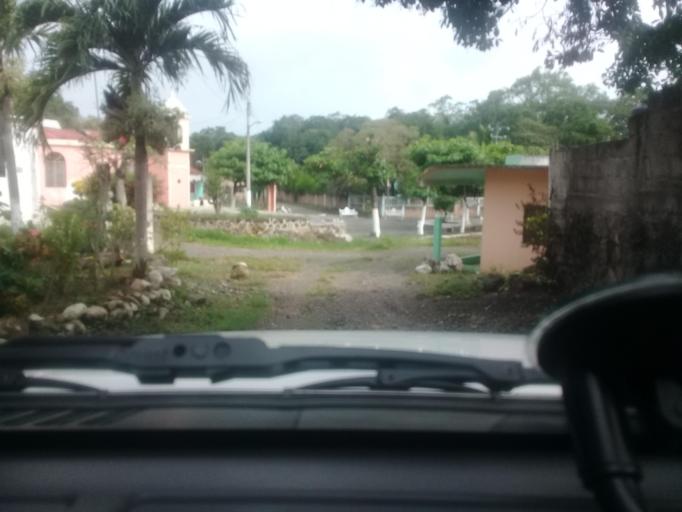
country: MX
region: Veracruz
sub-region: Paso de Ovejas
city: Tolome
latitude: 19.2623
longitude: -96.4120
